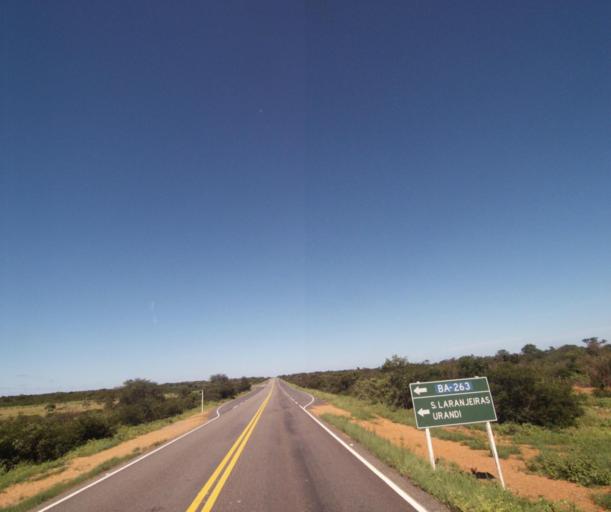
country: BR
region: Bahia
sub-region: Palmas De Monte Alto
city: Palmas de Monte Alto
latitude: -14.2510
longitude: -43.1814
